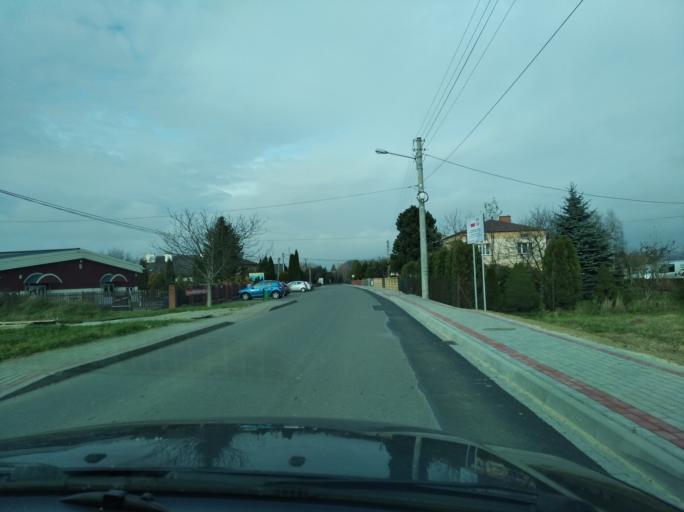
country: PL
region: Subcarpathian Voivodeship
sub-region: Powiat krosnienski
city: Kroscienko Wyzne
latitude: 49.6612
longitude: 21.8327
